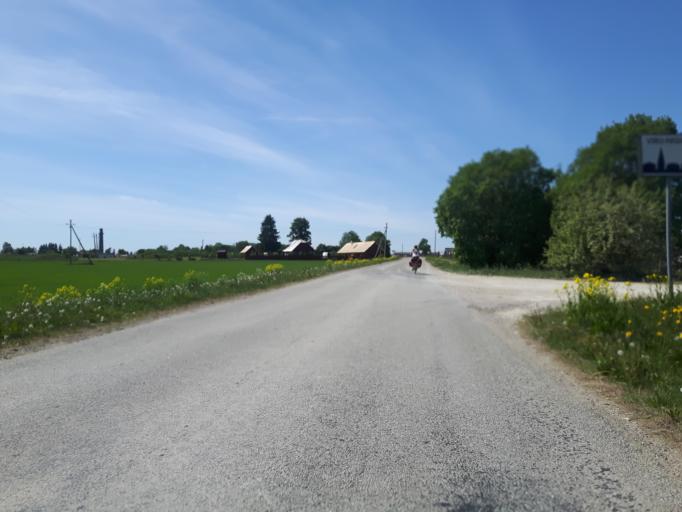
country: EE
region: Laeaene-Virumaa
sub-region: Viru-Nigula vald
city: Kunda
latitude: 59.4516
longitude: 26.6967
